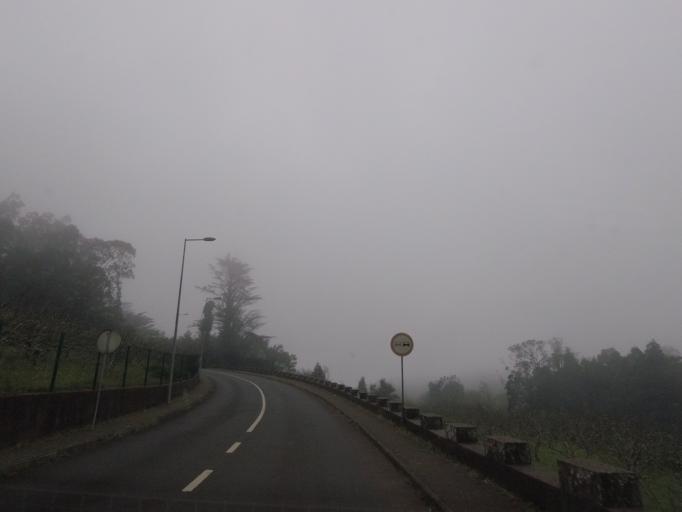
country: PT
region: Madeira
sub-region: Santa Cruz
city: Camacha
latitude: 32.7248
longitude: -16.8266
